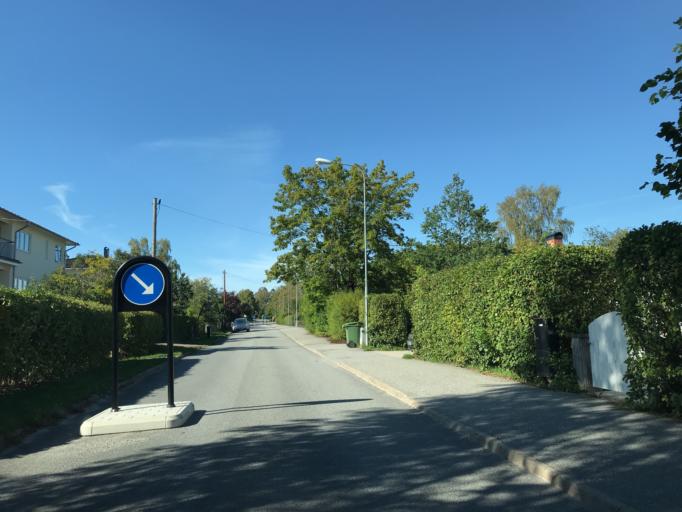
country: SE
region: Stockholm
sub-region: Sollentuna Kommun
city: Sollentuna
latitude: 59.4135
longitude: 17.9842
